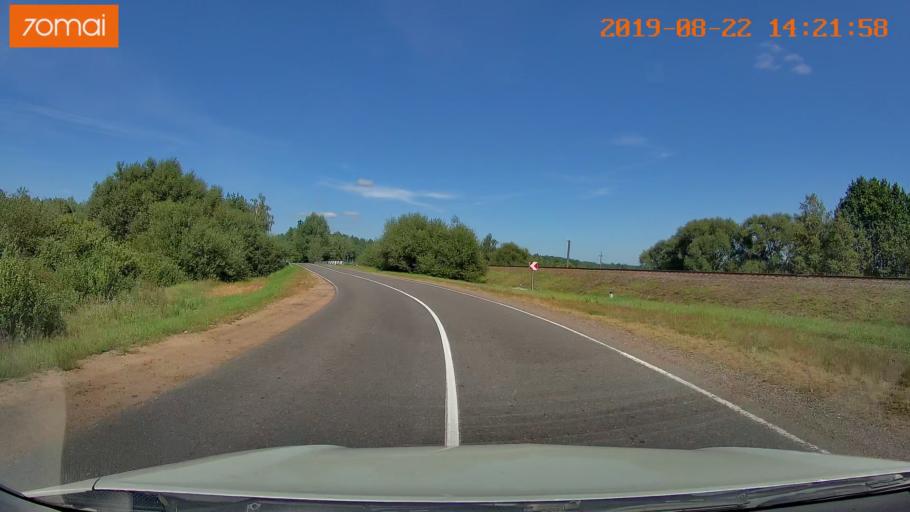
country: BY
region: Mogilev
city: Asipovichy
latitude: 53.2707
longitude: 28.5673
